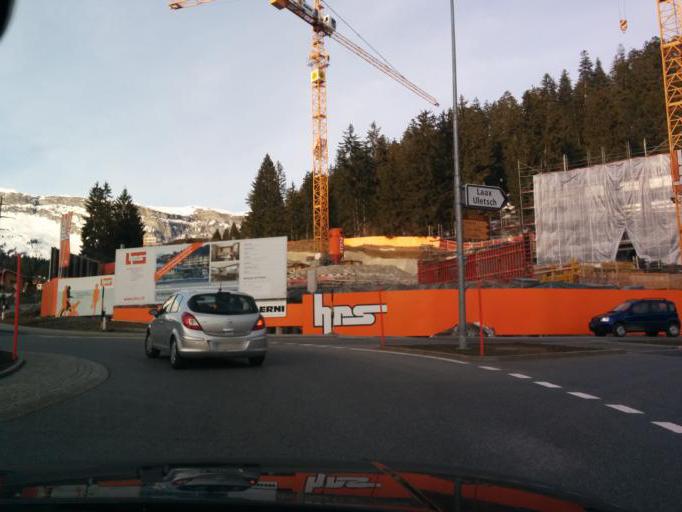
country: CH
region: Grisons
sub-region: Surselva District
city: Laax
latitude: 46.8166
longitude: 9.2667
